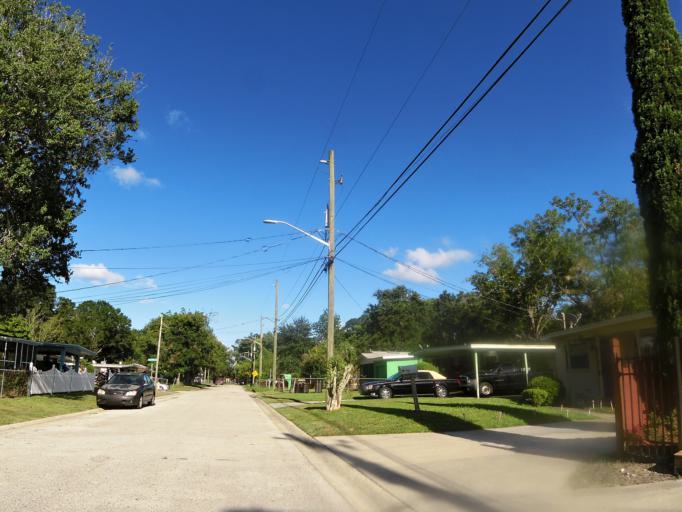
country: US
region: Florida
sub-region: Duval County
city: Jacksonville
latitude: 30.3526
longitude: -81.6963
